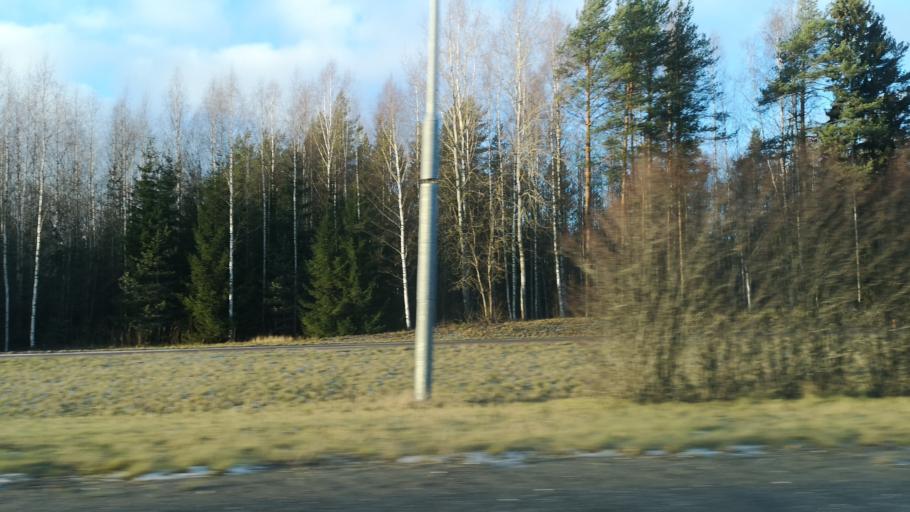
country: FI
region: Paijanne Tavastia
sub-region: Lahti
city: Heinola
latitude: 61.2576
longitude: 26.0579
